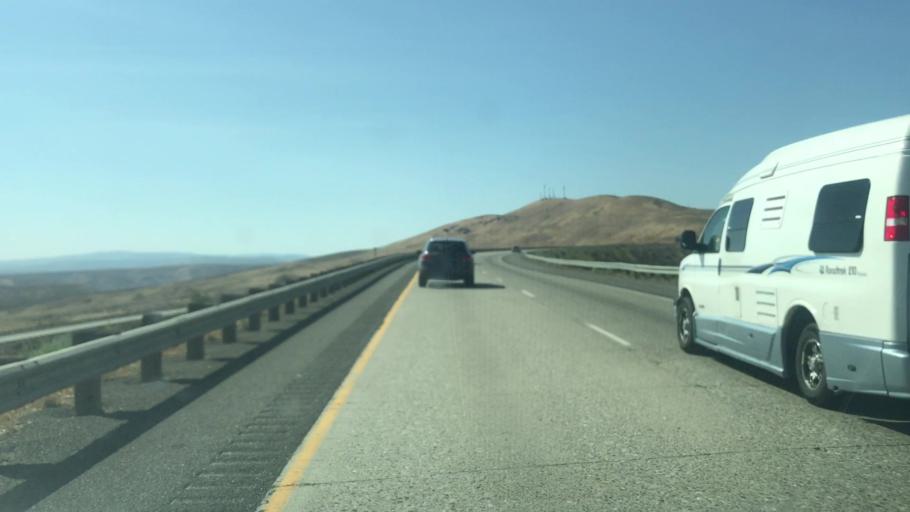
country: US
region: Washington
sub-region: Kittitas County
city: Kittitas
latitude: 46.8719
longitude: -120.4180
